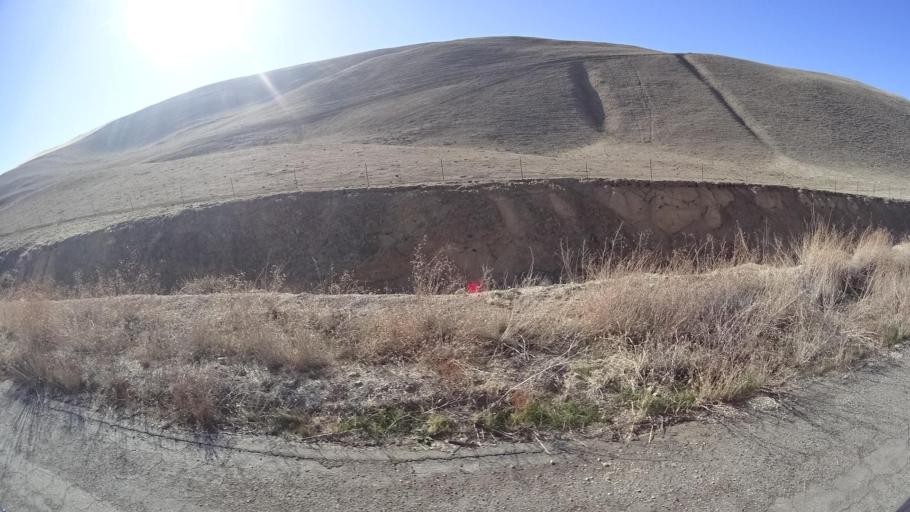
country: US
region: California
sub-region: Kern County
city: Maricopa
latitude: 34.9572
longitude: -119.4091
